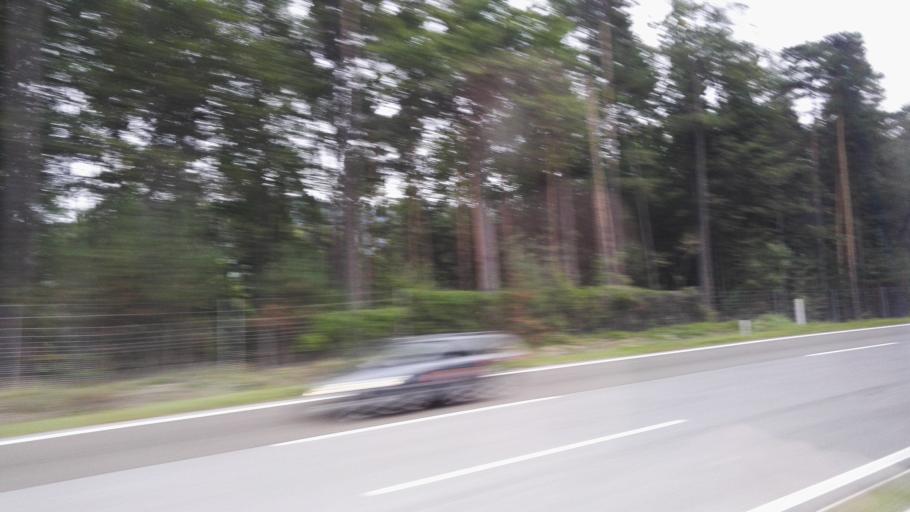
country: AT
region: Lower Austria
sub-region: Politischer Bezirk Neunkirchen
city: Schottwien
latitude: 47.6549
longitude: 15.8935
